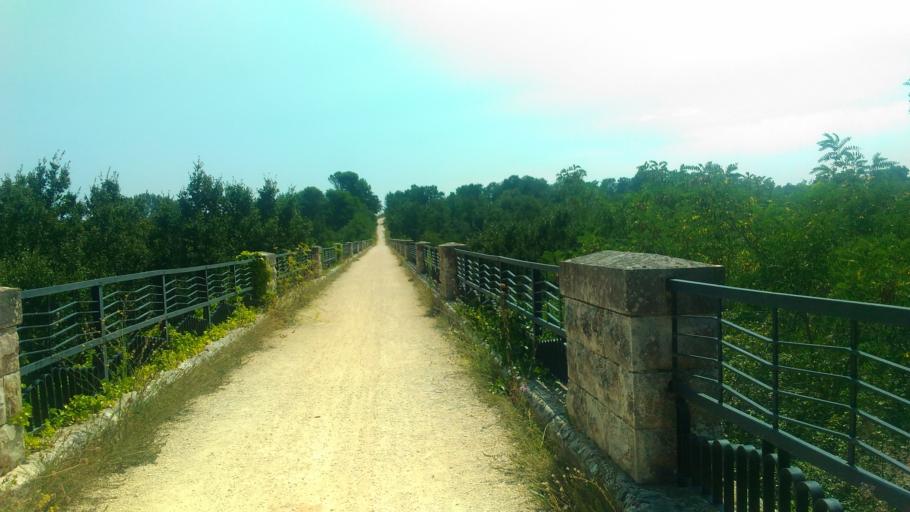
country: IT
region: Apulia
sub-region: Provincia di Brindisi
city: Cisternino
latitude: 40.7417
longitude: 17.3818
